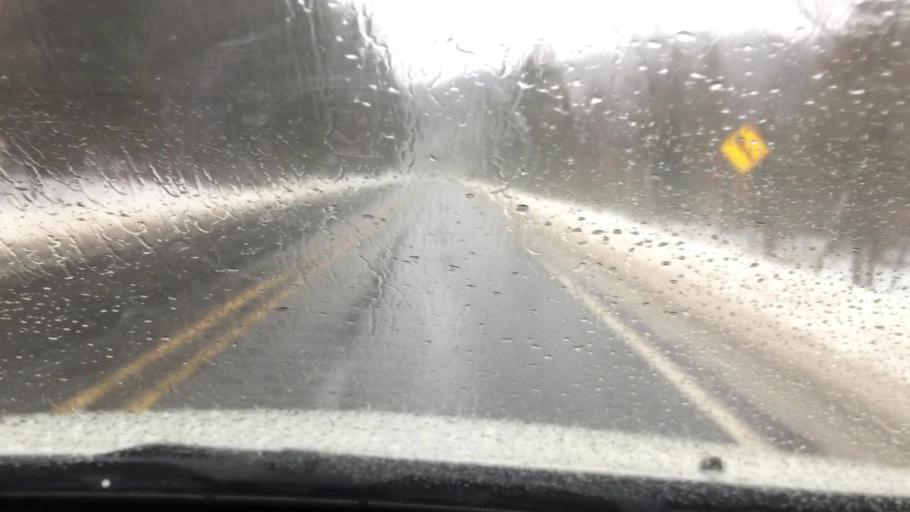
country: US
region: Michigan
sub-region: Antrim County
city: Mancelona
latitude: 45.0040
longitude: -85.0629
